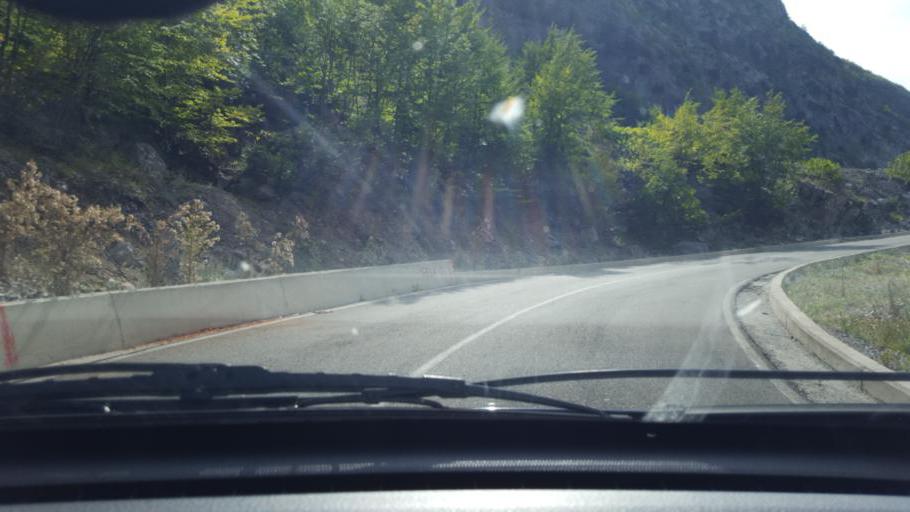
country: ME
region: Andrijevica
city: Andrijevica
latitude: 42.5328
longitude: 19.6581
